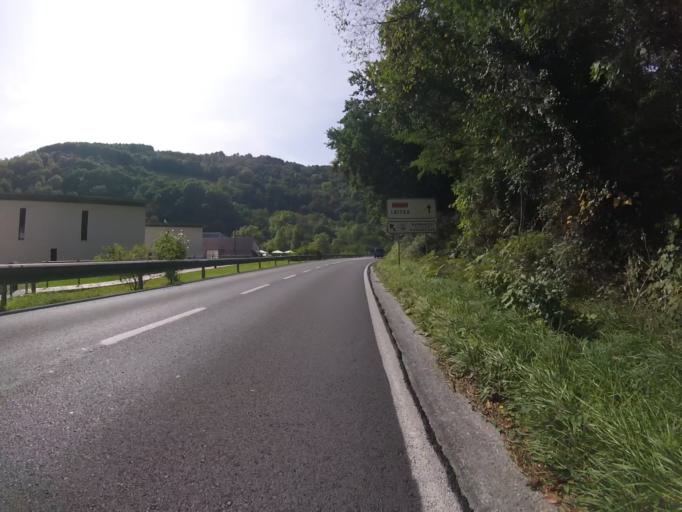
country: ES
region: Navarre
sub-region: Provincia de Navarra
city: Elgorriaga
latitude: 43.1354
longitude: -1.6904
